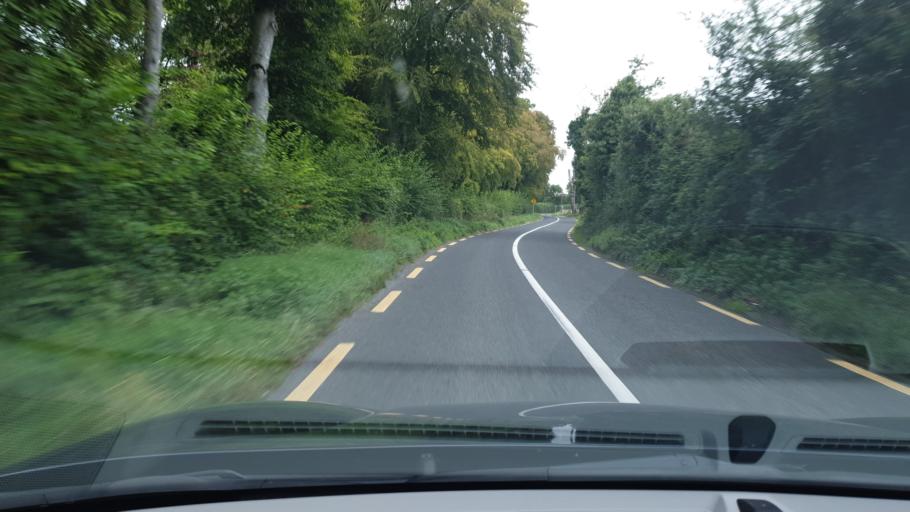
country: IE
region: Leinster
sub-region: Kildare
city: Kilcock
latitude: 53.4165
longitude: -6.6603
